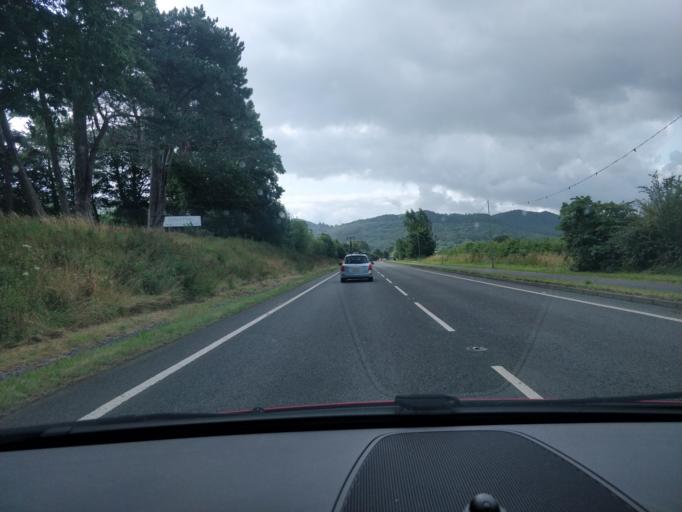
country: GB
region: Wales
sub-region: Conwy
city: Llanrwst
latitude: 53.1202
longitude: -3.7814
